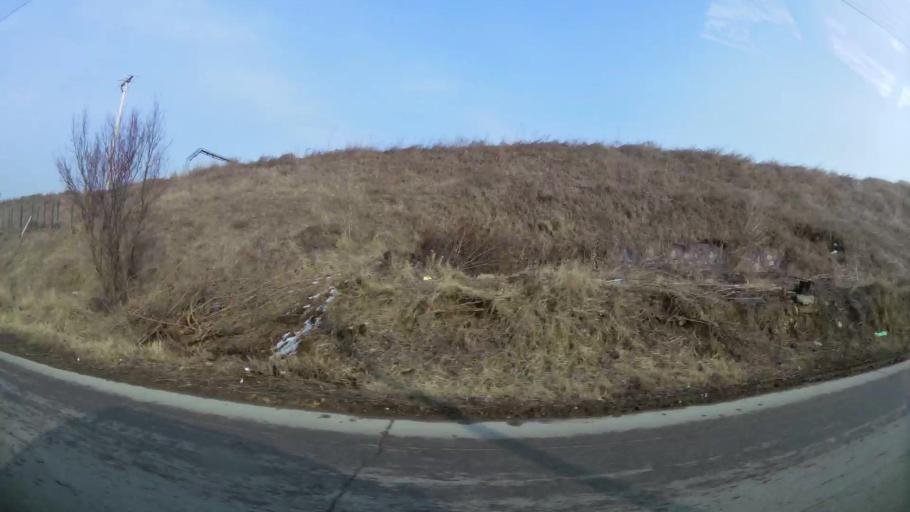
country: MK
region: Ilinden
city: Marino
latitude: 41.9858
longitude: 21.5942
